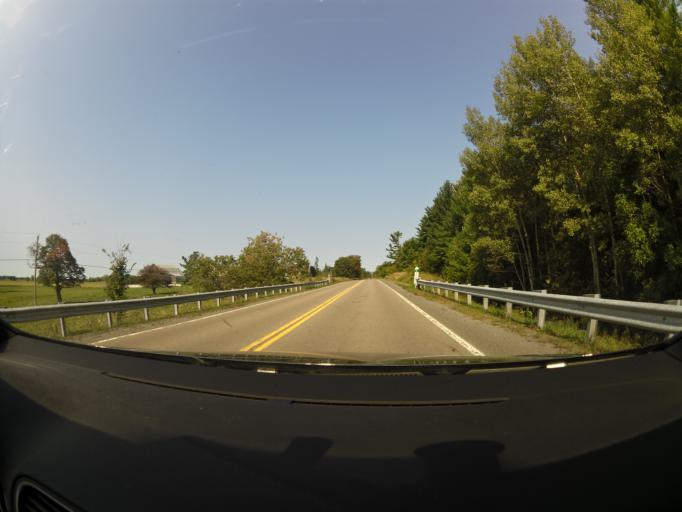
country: CA
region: Ontario
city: Arnprior
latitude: 45.4410
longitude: -76.1810
